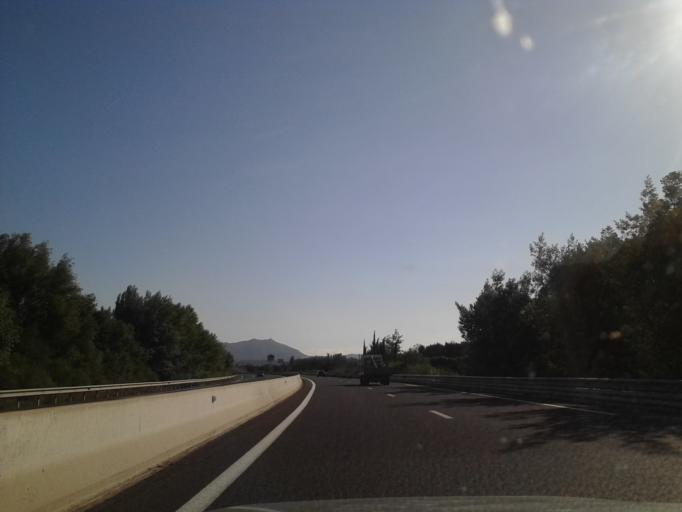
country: FR
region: Languedoc-Roussillon
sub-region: Departement des Pyrenees-Orientales
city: Ille-sur-Tet
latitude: 42.6759
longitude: 2.6244
